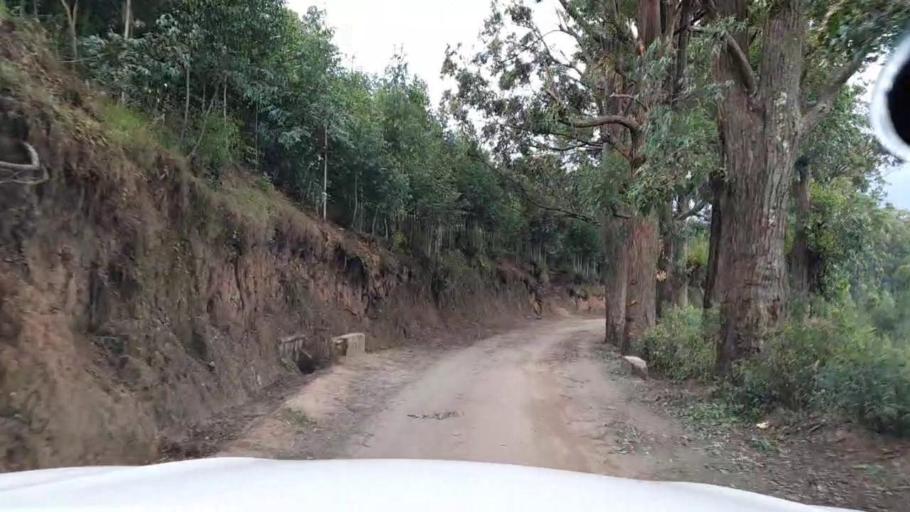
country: BI
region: Kayanza
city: Kayanza
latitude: -2.7956
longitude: 29.5092
